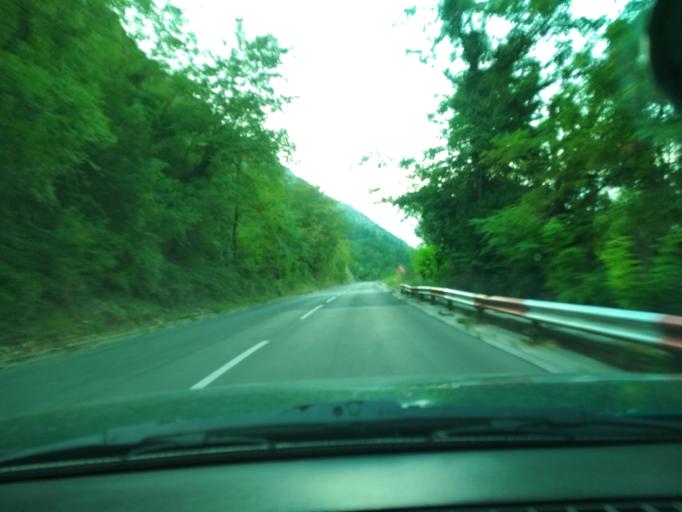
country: ME
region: Kotor
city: Kotor
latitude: 42.4169
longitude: 18.7599
